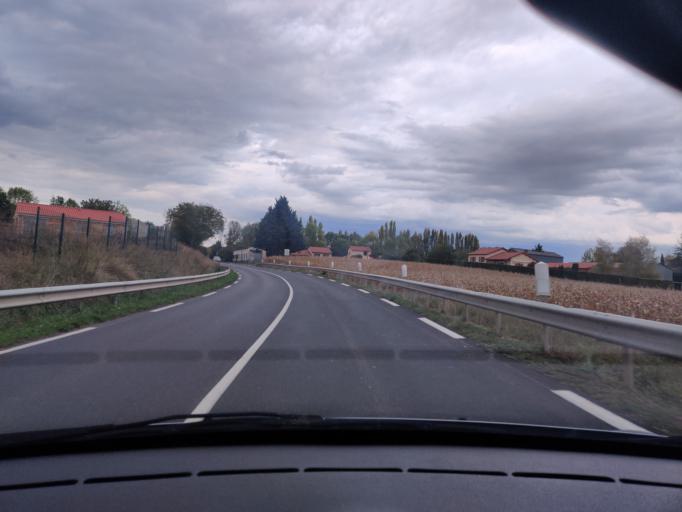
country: FR
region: Auvergne
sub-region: Departement du Puy-de-Dome
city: Saint-Bonnet-pres-Riom
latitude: 45.9433
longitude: 3.1109
